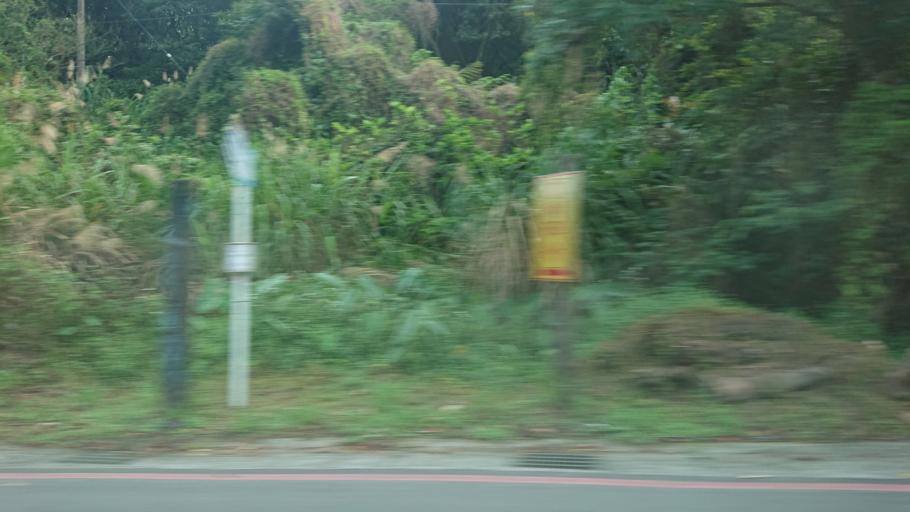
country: TW
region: Taiwan
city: Daxi
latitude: 24.8688
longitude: 121.4124
